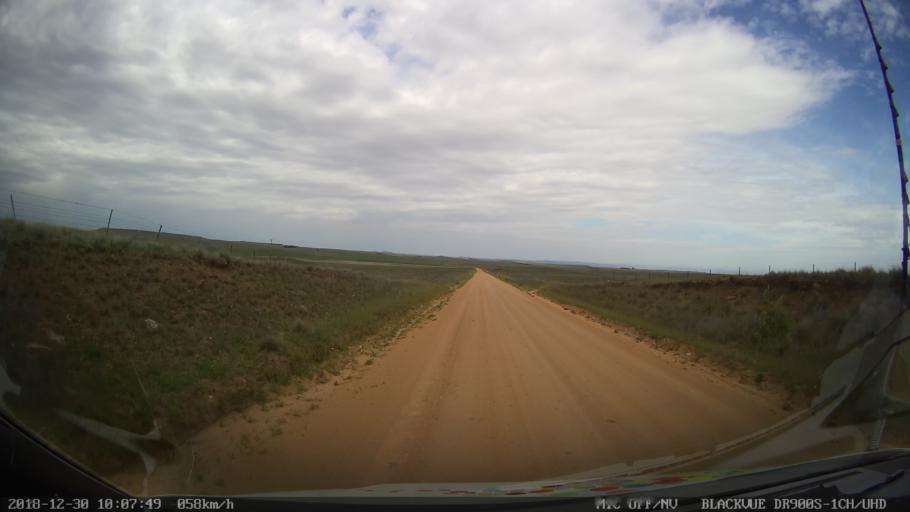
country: AU
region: New South Wales
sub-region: Cooma-Monaro
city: Cooma
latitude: -36.5417
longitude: 149.1195
